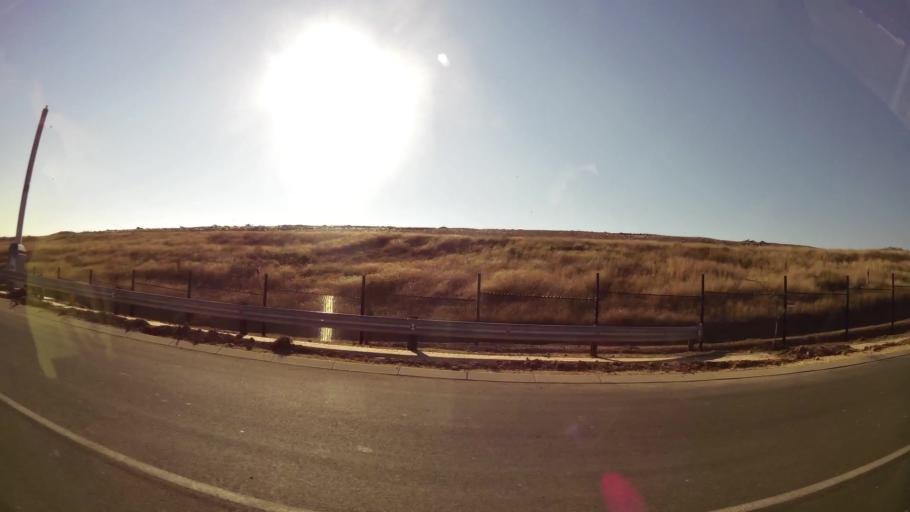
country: ZA
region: Gauteng
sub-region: City of Johannesburg Metropolitan Municipality
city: Modderfontein
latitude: -26.0454
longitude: 28.1664
